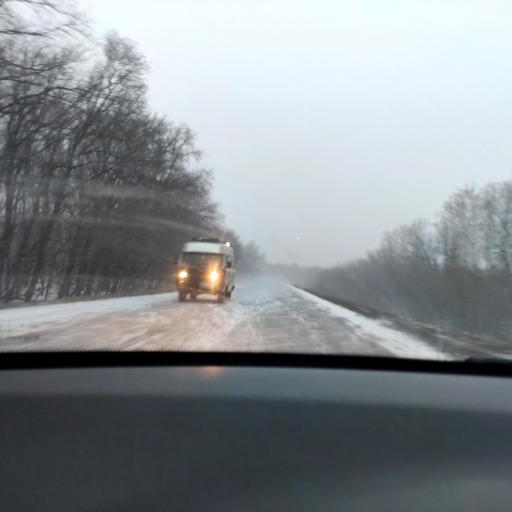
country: RU
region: Samara
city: Novokuybyshevsk
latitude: 52.9702
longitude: 49.8879
